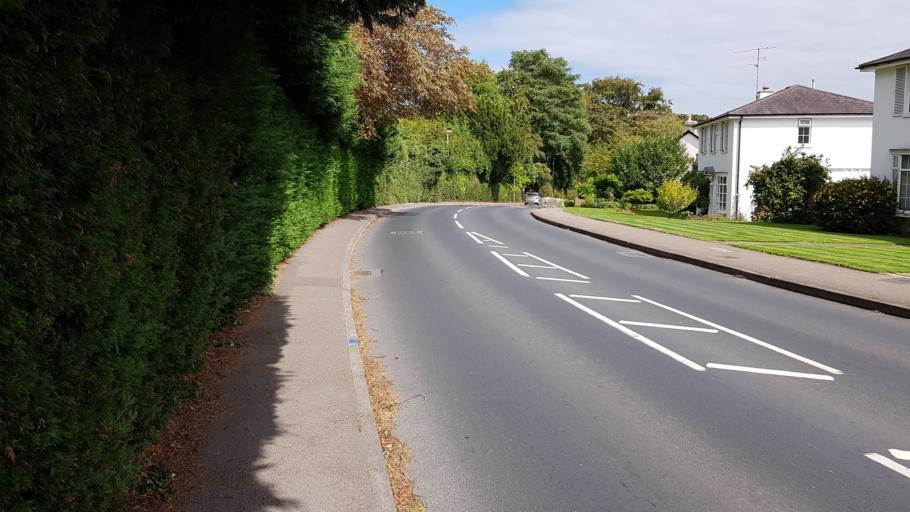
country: GB
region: England
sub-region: Gloucestershire
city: Charlton Kings
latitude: 51.8827
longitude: -2.0634
